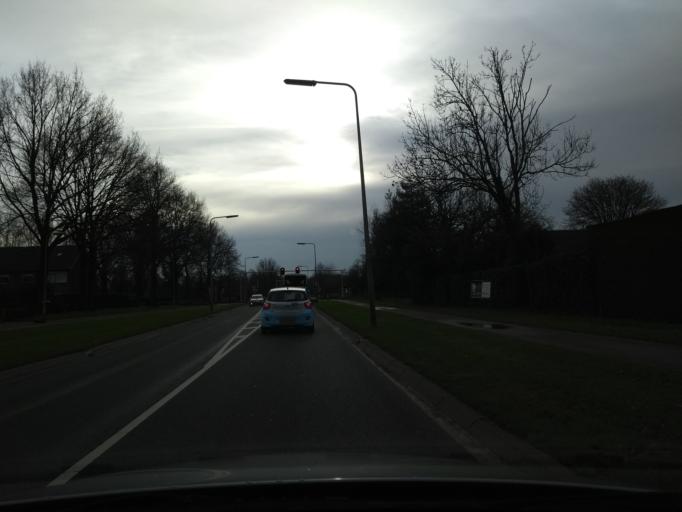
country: NL
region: Overijssel
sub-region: Gemeente Hof van Twente
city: Delden
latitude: 52.2594
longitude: 6.7017
